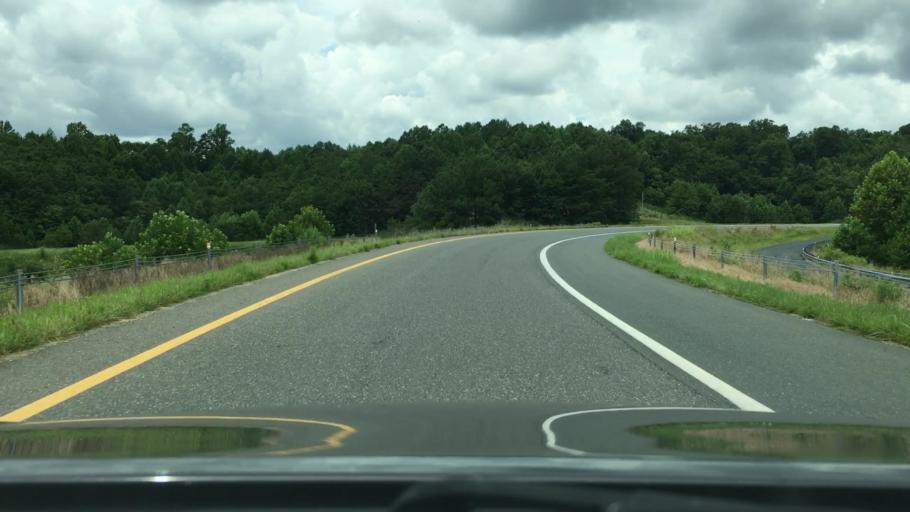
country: US
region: Virginia
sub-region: Amherst County
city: Madison Heights
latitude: 37.4099
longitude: -79.0810
